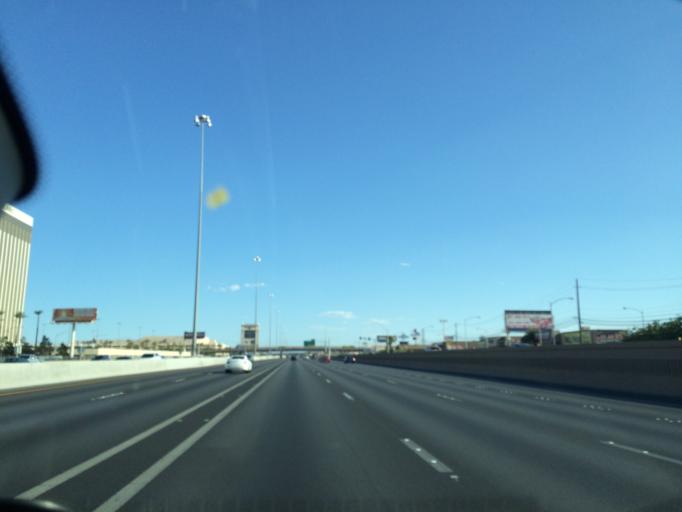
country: US
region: Nevada
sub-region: Clark County
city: Paradise
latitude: 36.0986
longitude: -115.1808
